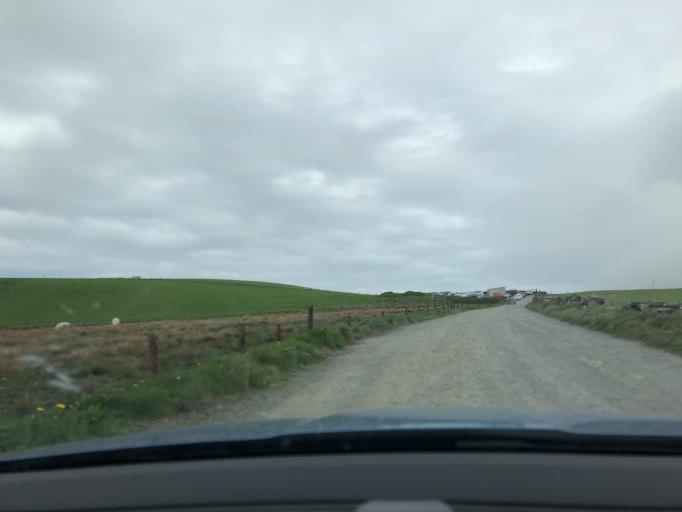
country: IE
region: Munster
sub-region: An Clar
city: Kilrush
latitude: 52.9621
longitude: -9.4313
